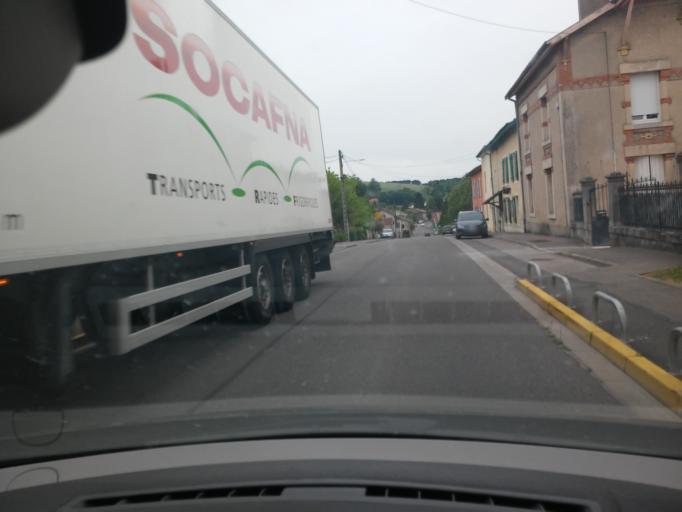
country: FR
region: Lorraine
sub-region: Departement de la Meuse
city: Lerouville
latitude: 48.8278
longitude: 5.5095
